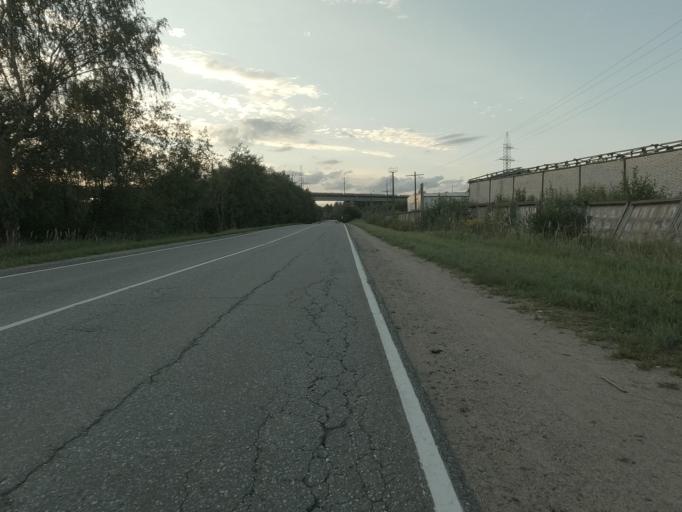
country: RU
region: Leningrad
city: Mga
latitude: 59.7570
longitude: 31.0205
